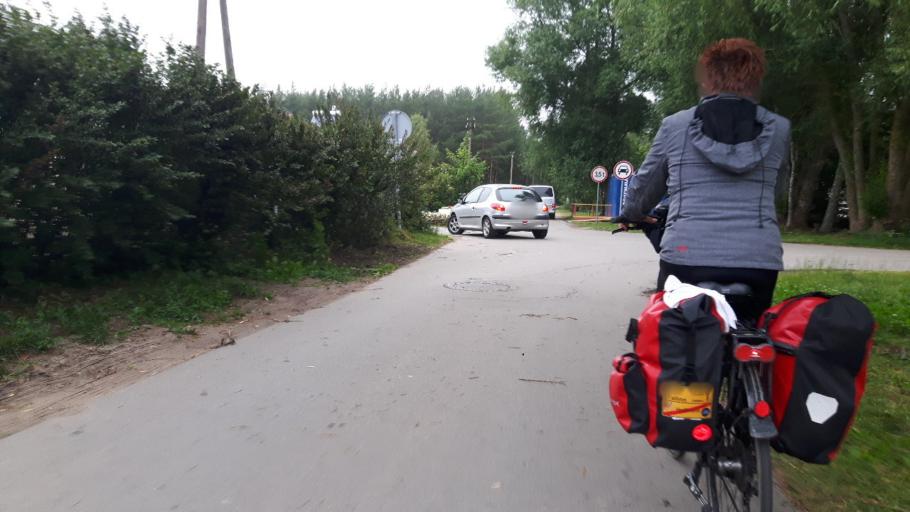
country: LT
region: Klaipedos apskritis
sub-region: Palanga
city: Sventoji
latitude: 56.0034
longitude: 21.0764
